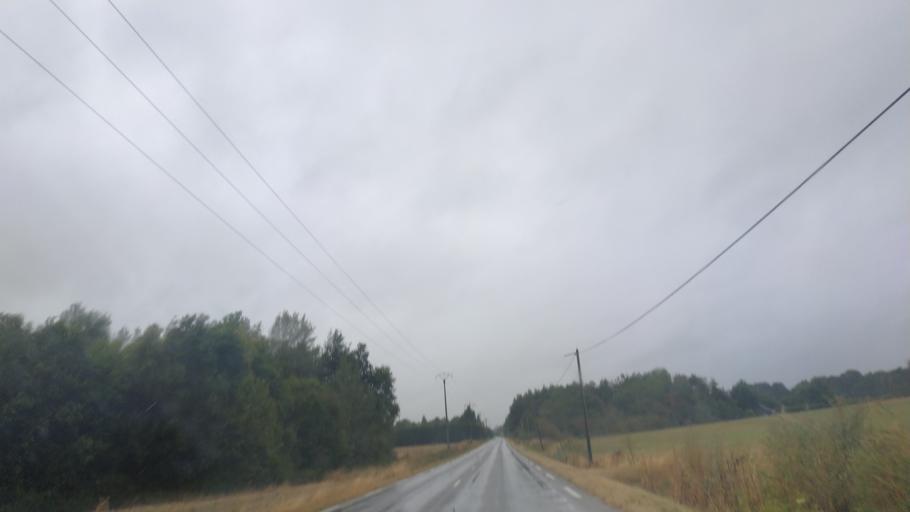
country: FR
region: Centre
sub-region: Departement du Loiret
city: Bellegarde
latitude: 47.9320
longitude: 2.3907
